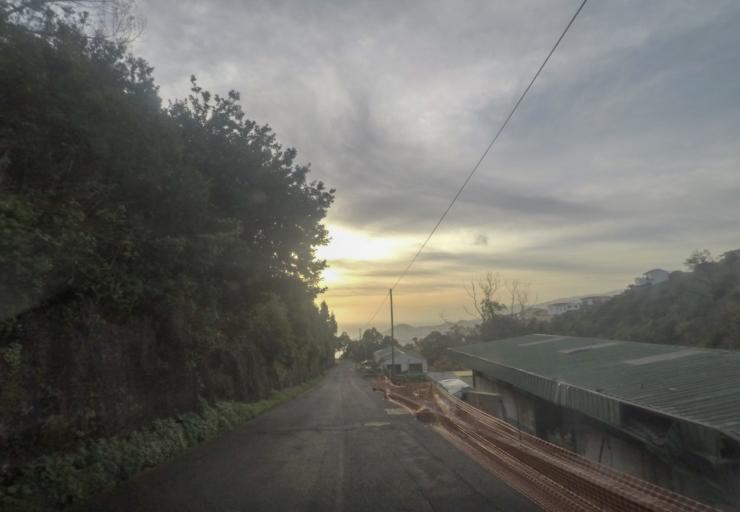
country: PT
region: Madeira
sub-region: Funchal
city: Nossa Senhora do Monte
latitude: 32.6589
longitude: -16.8737
